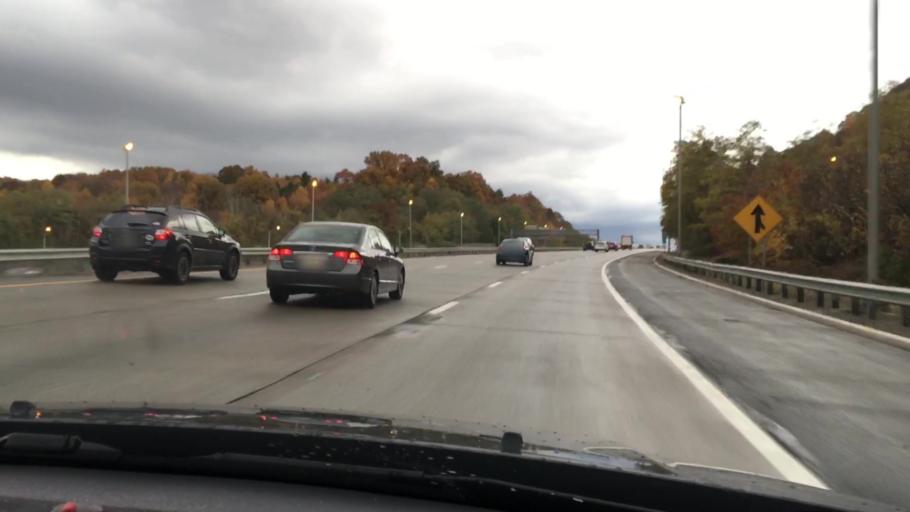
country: US
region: New Jersey
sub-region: Morris County
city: Riverdale
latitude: 40.9875
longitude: -74.3099
